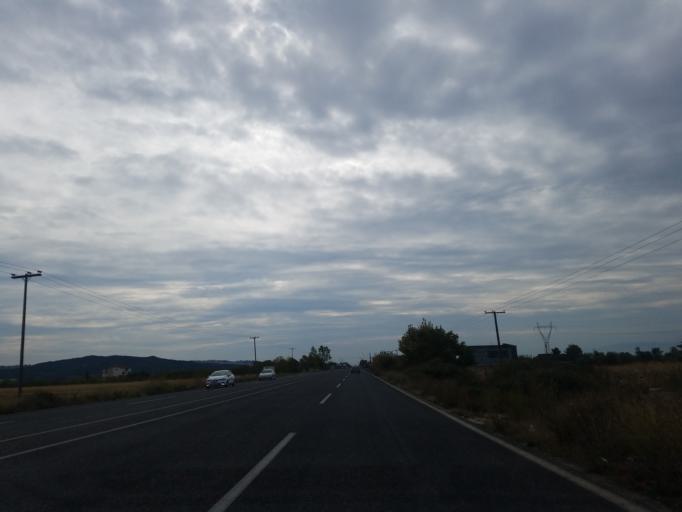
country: GR
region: Thessaly
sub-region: Trikala
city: Kalampaka
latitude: 39.6780
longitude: 21.6578
